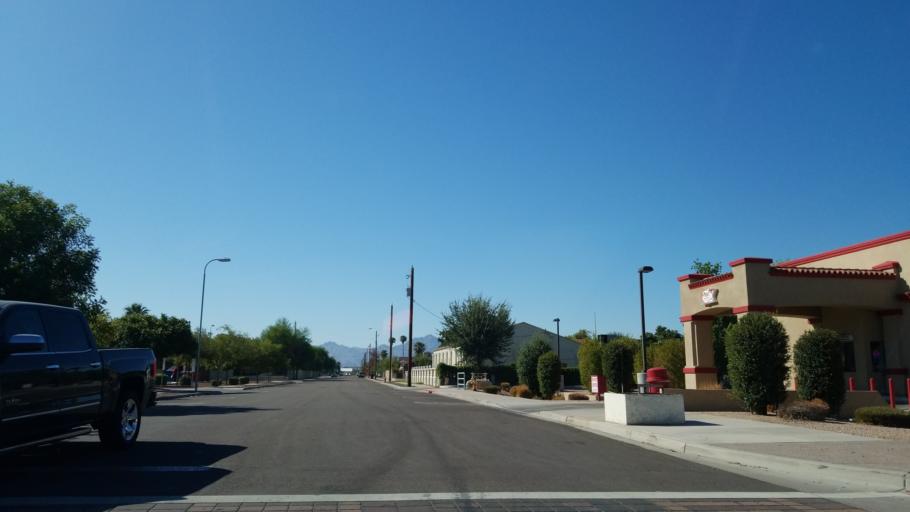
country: US
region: Arizona
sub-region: Maricopa County
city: Tolleson
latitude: 33.4503
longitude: -112.2600
